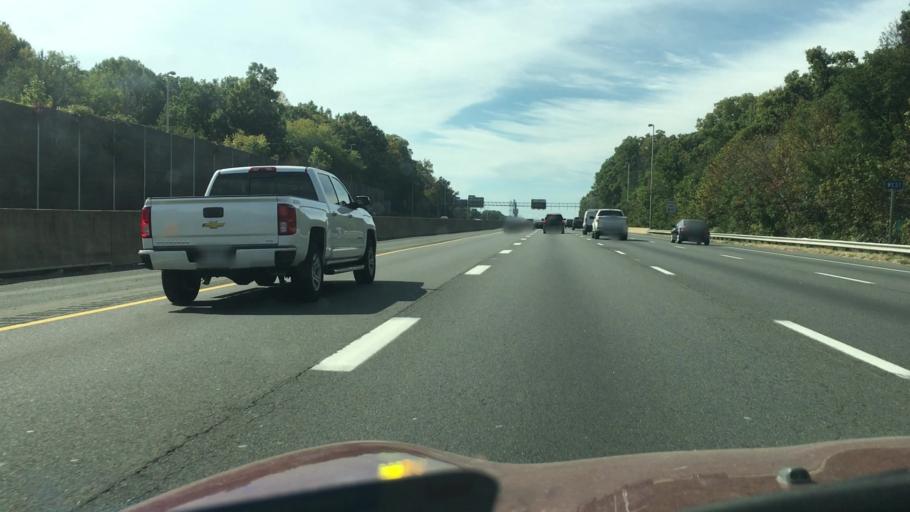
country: US
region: Virginia
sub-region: Fairfax County
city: Centreville
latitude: 38.8320
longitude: -77.4519
